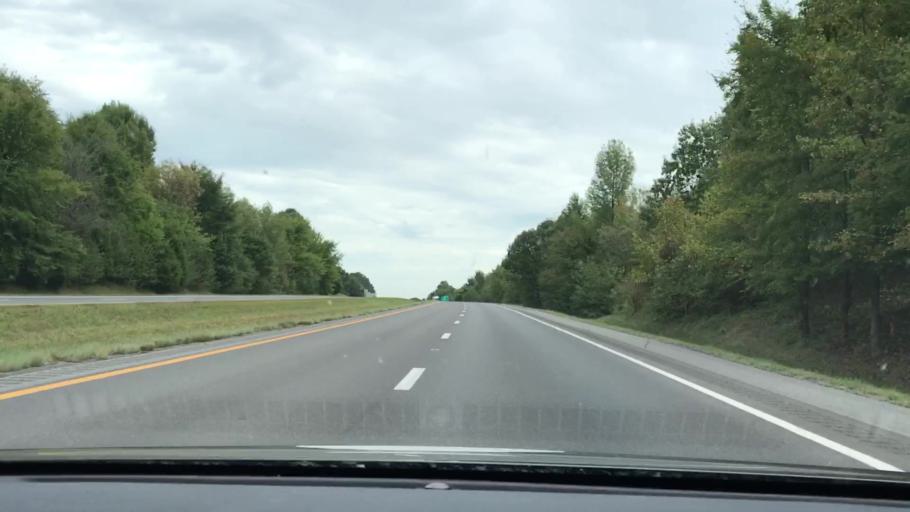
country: US
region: Kentucky
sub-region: Graves County
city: Mayfield
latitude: 36.7711
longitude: -88.6082
